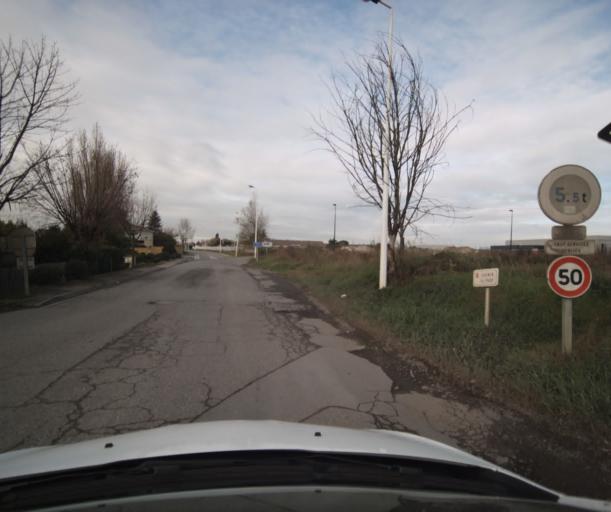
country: FR
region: Midi-Pyrenees
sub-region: Departement de la Haute-Garonne
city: Lespinasse
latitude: 43.7126
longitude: 1.3974
